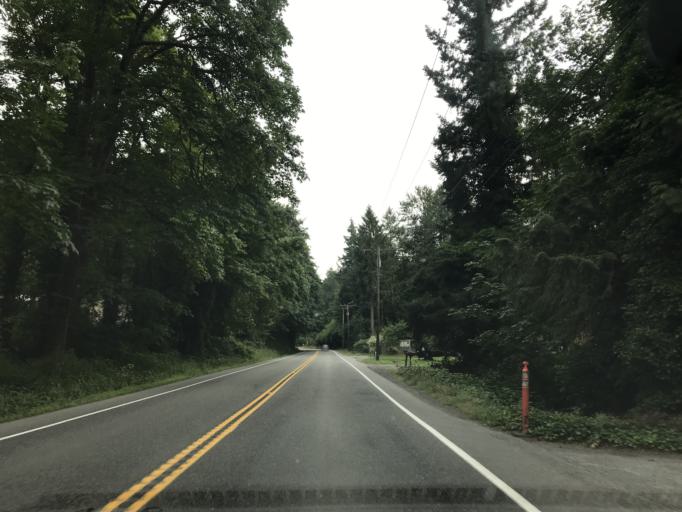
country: US
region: Washington
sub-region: King County
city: Fall City
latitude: 47.5576
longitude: -121.8970
